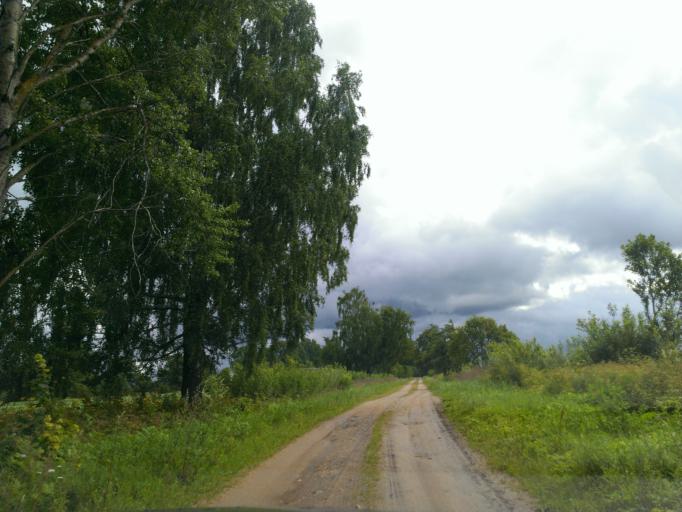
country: LV
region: Ligatne
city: Ligatne
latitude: 57.2069
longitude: 24.9509
